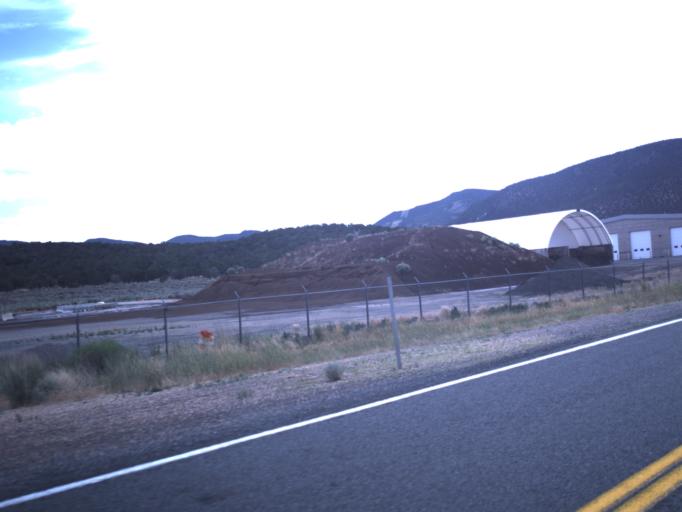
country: US
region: Utah
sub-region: Beaver County
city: Beaver
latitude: 38.6040
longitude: -112.5837
